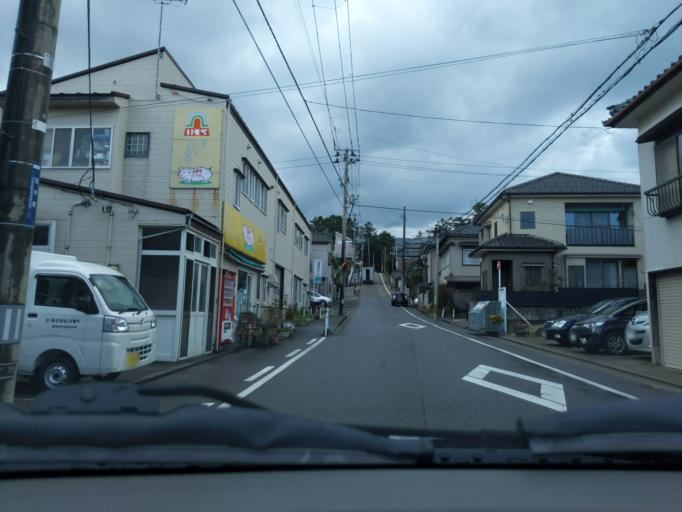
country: JP
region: Niigata
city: Niigata-shi
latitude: 37.9301
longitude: 139.0422
